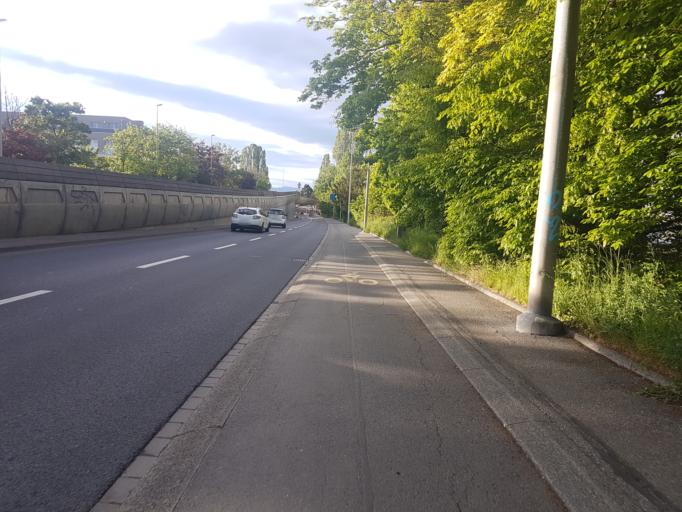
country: CH
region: Geneva
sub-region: Geneva
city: Les Avanchets
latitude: 46.2088
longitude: 6.1097
